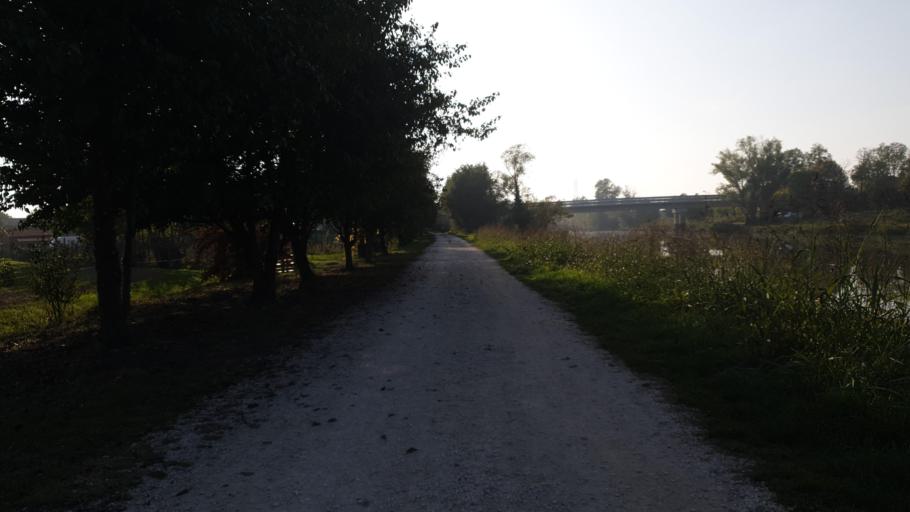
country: IT
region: Veneto
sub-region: Provincia di Venezia
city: Tombelle
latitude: 45.3854
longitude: 11.9863
